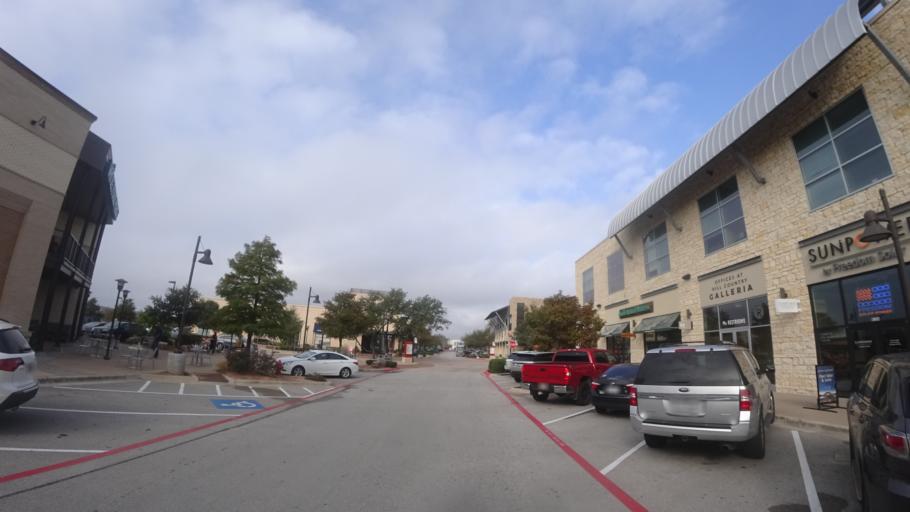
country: US
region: Texas
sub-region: Travis County
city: Bee Cave
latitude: 30.3080
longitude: -97.9377
